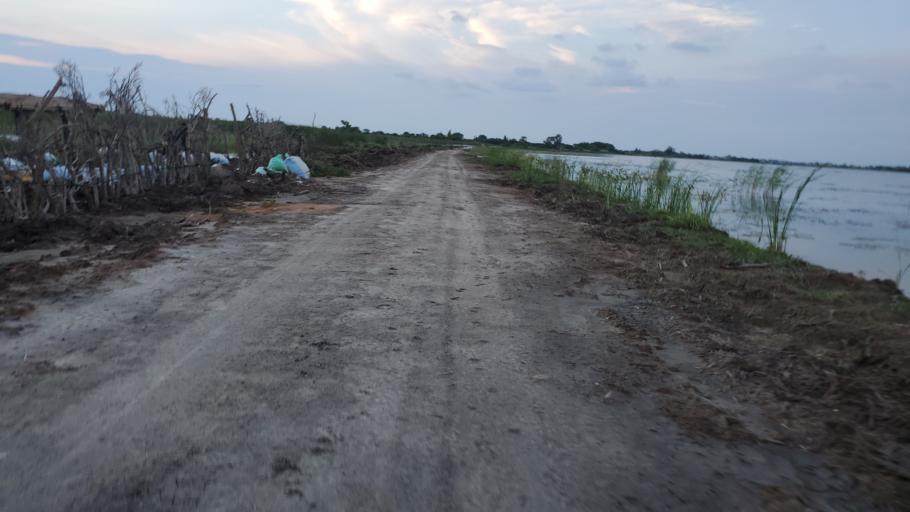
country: SN
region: Saint-Louis
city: Saint-Louis
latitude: 16.0331
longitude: -16.4145
